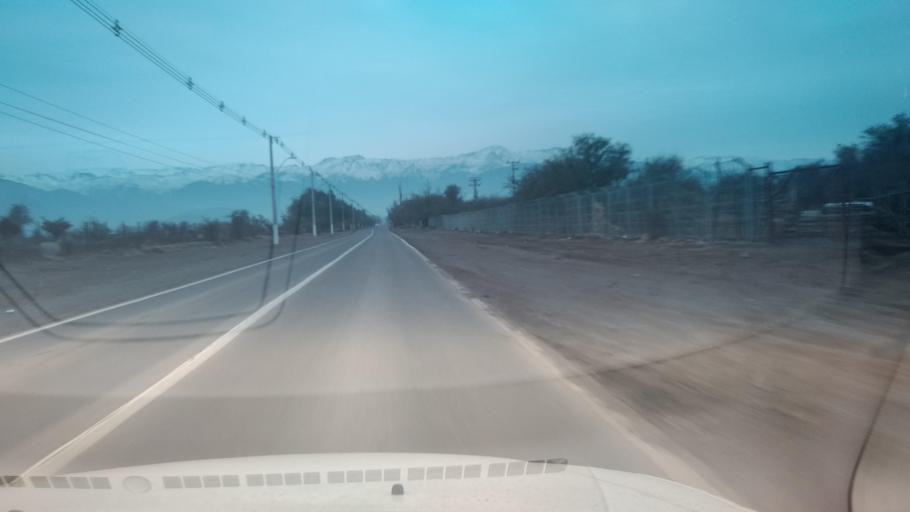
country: CL
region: Santiago Metropolitan
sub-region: Provincia de Chacabuco
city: Chicureo Abajo
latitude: -33.0923
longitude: -70.7260
